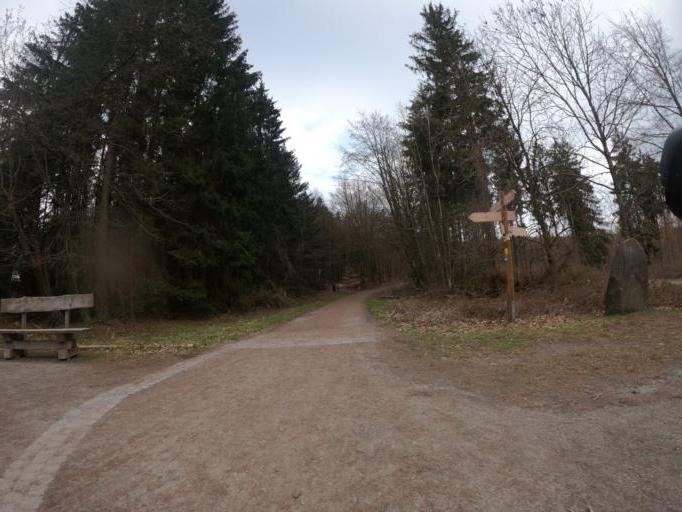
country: DE
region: North Rhine-Westphalia
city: Heimbach
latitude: 50.6170
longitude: 6.4272
